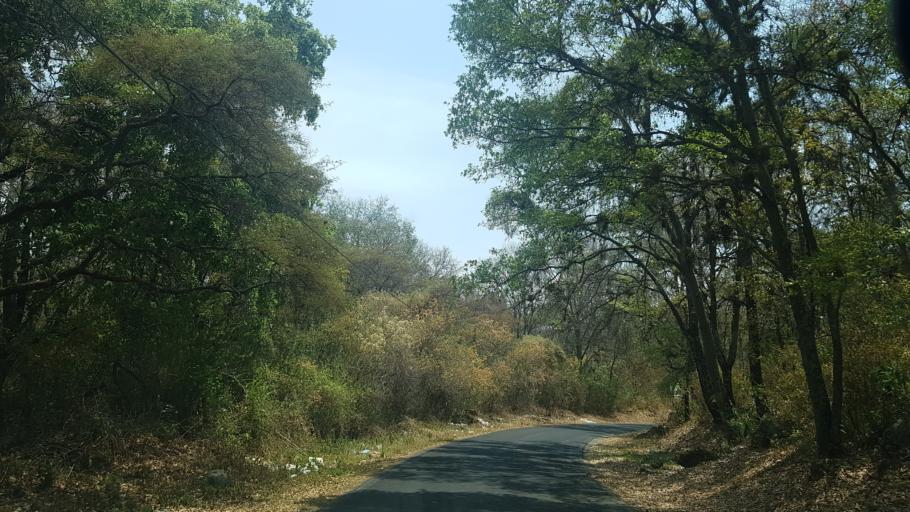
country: MX
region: Puebla
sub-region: Tochimilco
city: La Magdalena Yancuitlalpan
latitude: 18.8860
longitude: -98.5928
